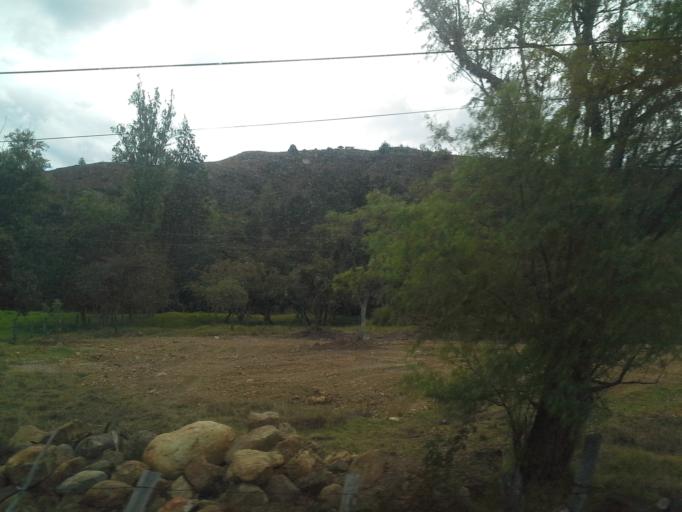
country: CO
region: Boyaca
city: Raquira
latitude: 5.5458
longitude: -73.6368
